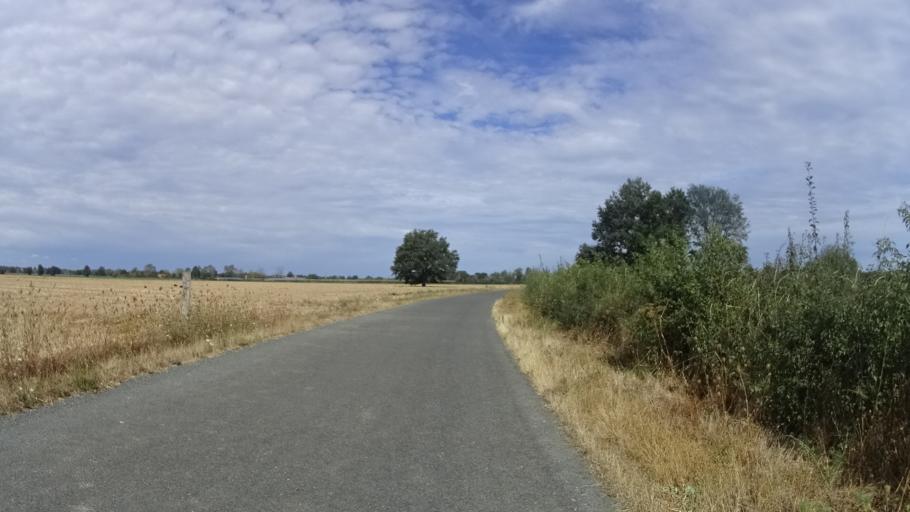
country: FR
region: Auvergne
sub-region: Departement de l'Allier
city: Beaulon
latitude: 46.6397
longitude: 3.6925
